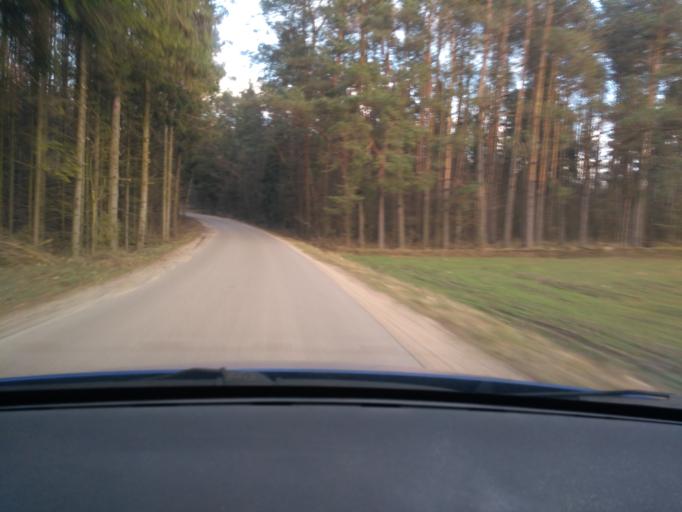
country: PL
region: Pomeranian Voivodeship
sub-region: Powiat kartuski
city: Przodkowo
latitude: 54.4127
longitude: 18.2590
